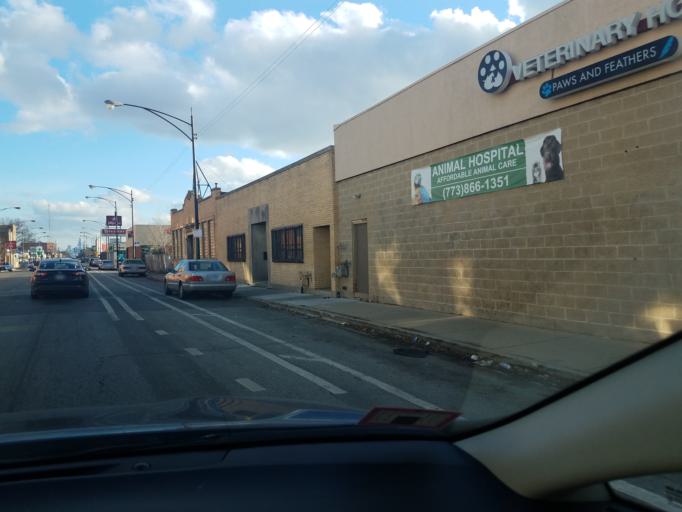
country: US
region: Illinois
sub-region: Cook County
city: Lincolnwood
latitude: 41.9481
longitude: -87.7111
